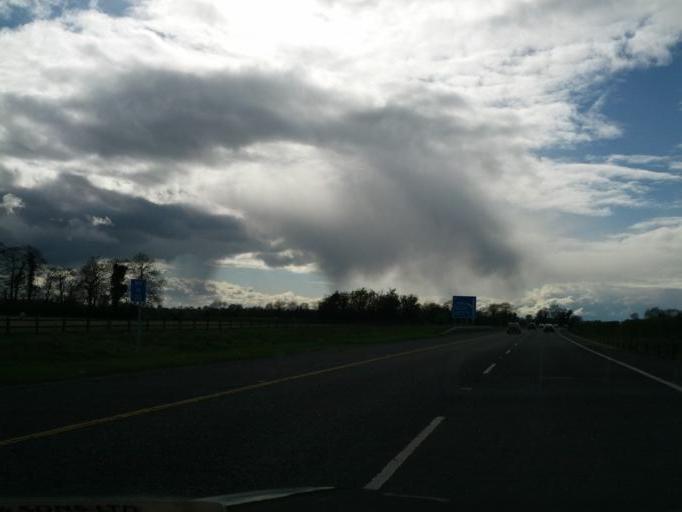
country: IE
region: Leinster
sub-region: An Mhi
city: Enfield
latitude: 53.4042
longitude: -6.8210
